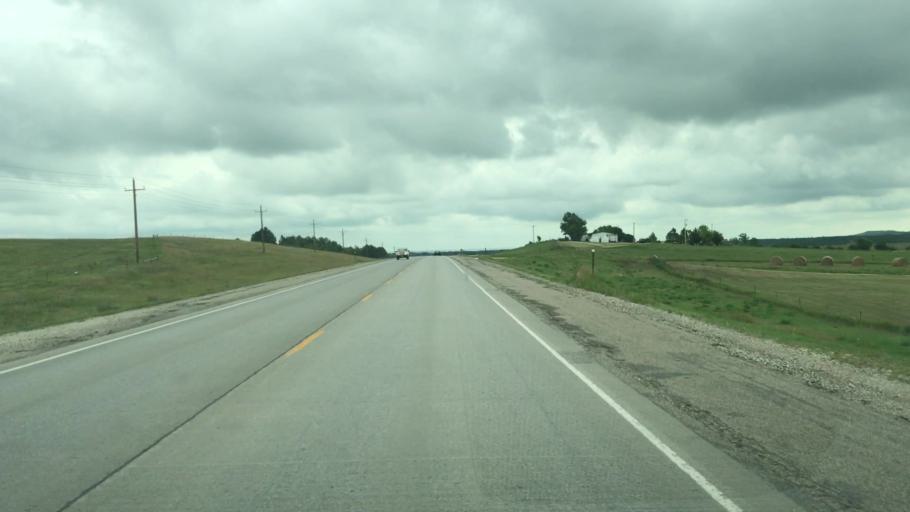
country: US
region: South Dakota
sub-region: Todd County
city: Mission
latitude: 43.3029
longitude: -100.6978
